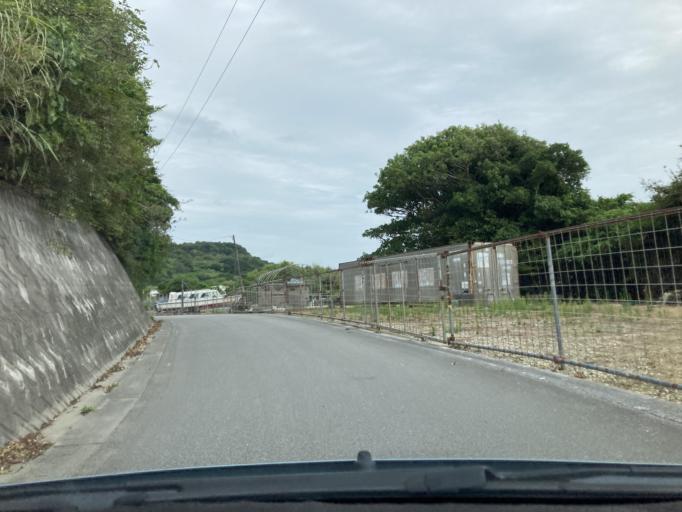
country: JP
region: Okinawa
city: Tomigusuku
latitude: 26.1352
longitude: 127.7924
